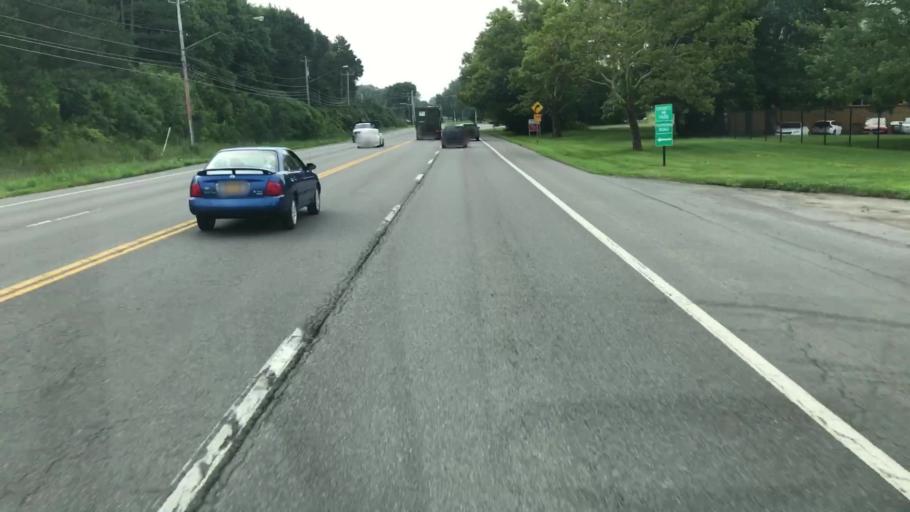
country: US
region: New York
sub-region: Onondaga County
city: Galeville
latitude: 43.1109
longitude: -76.1842
